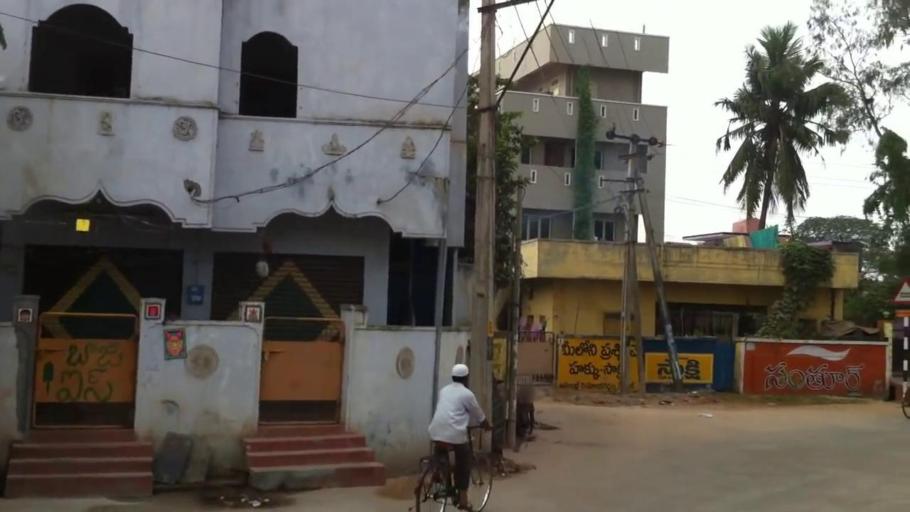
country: IN
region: Andhra Pradesh
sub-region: Guntur
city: Bhattiprolu
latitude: 16.2268
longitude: 80.6529
